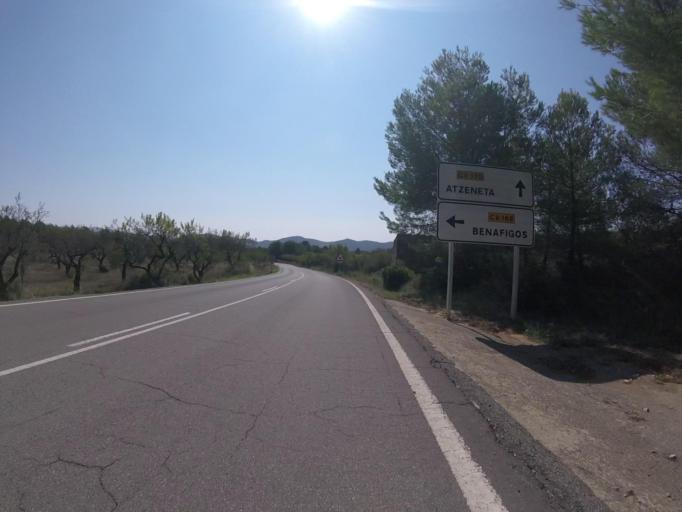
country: ES
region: Valencia
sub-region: Provincia de Castello
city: Adzaneta
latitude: 40.2354
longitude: -0.1814
